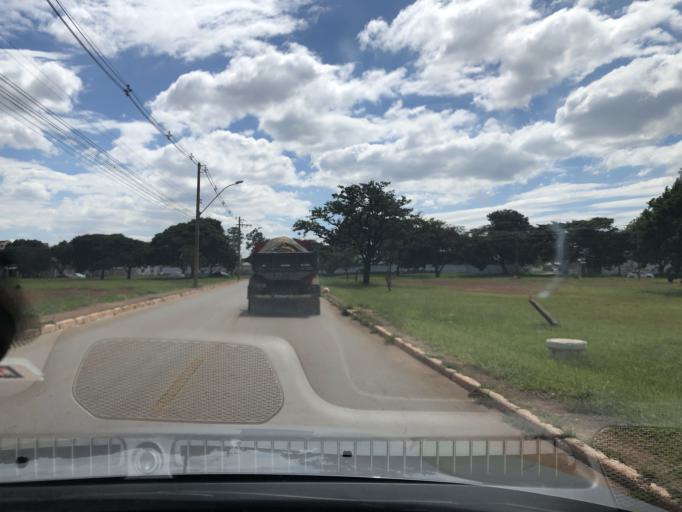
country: BR
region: Federal District
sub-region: Brasilia
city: Brasilia
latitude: -16.0012
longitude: -48.0562
